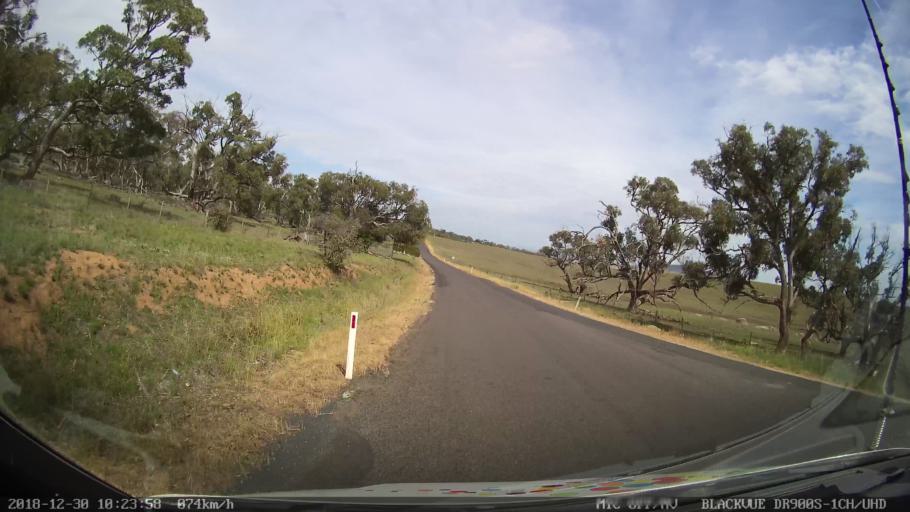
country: AU
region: New South Wales
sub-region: Snowy River
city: Berridale
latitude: -36.5330
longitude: 148.9764
